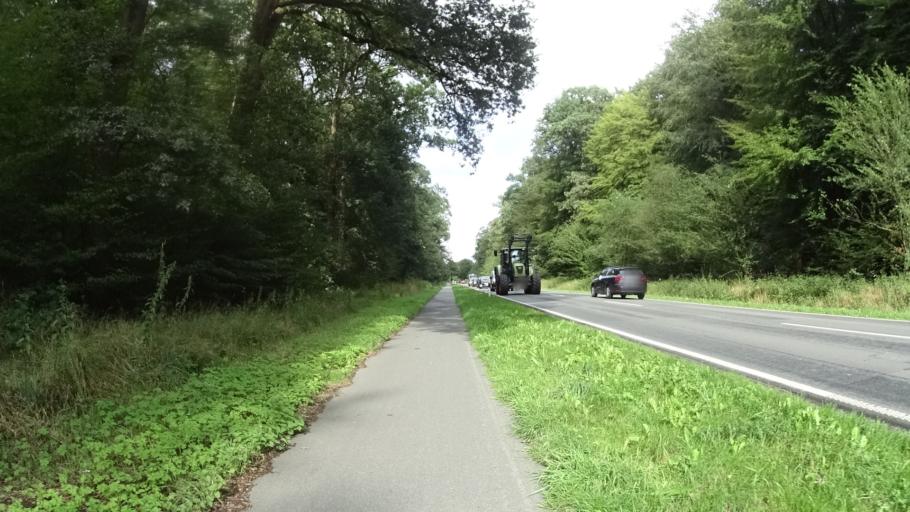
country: DE
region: Lower Saxony
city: Varel
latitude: 53.3876
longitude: 8.0781
